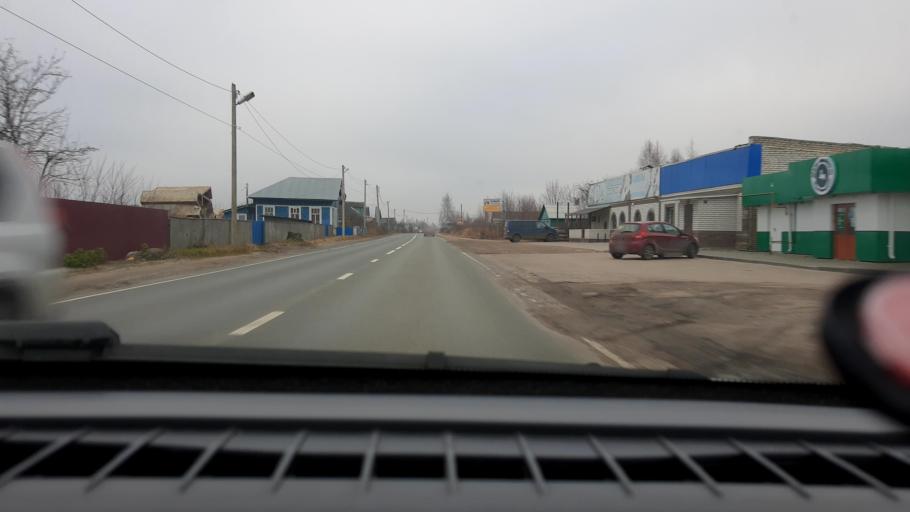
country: RU
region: Nizjnij Novgorod
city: Gidrotorf
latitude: 56.5478
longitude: 43.5244
